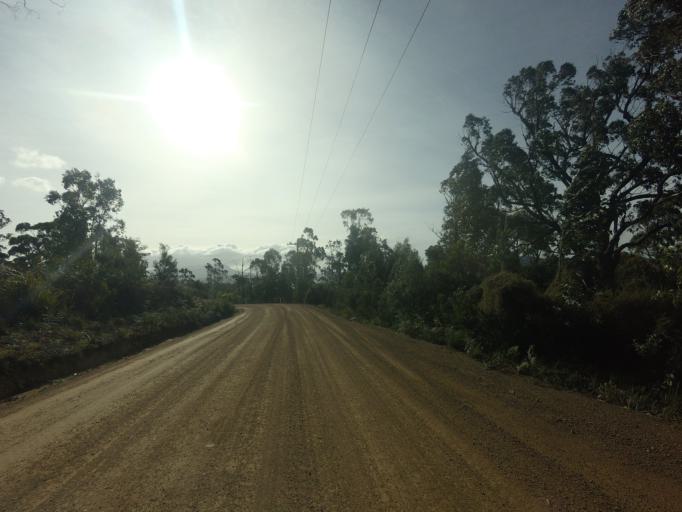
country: AU
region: Tasmania
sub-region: Kingborough
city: Kettering
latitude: -43.0828
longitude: 147.2647
